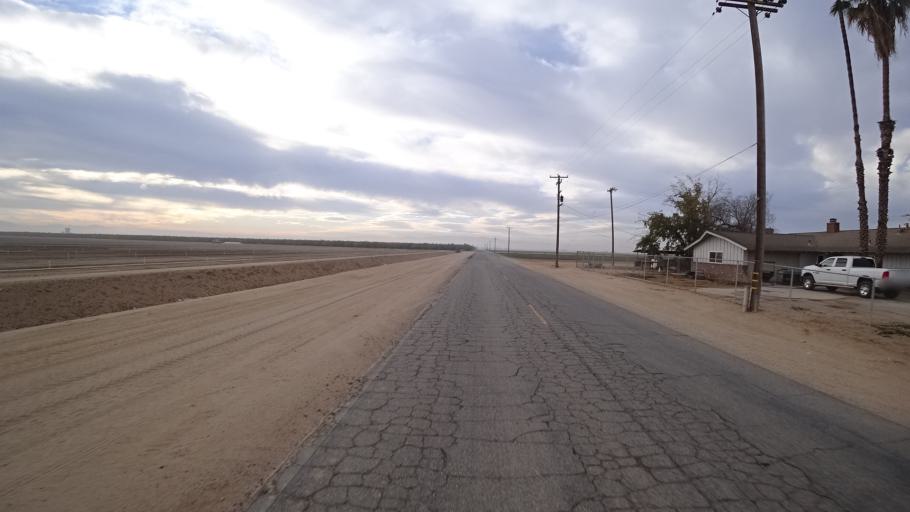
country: US
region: California
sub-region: Kern County
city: Rosedale
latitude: 35.4152
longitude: -119.1987
